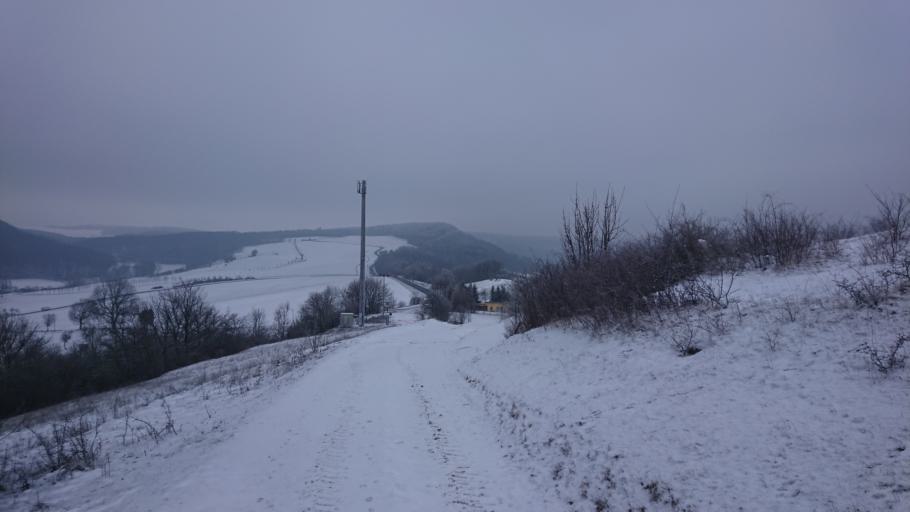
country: DE
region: Thuringia
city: Brehme
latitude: 51.4959
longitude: 10.3870
